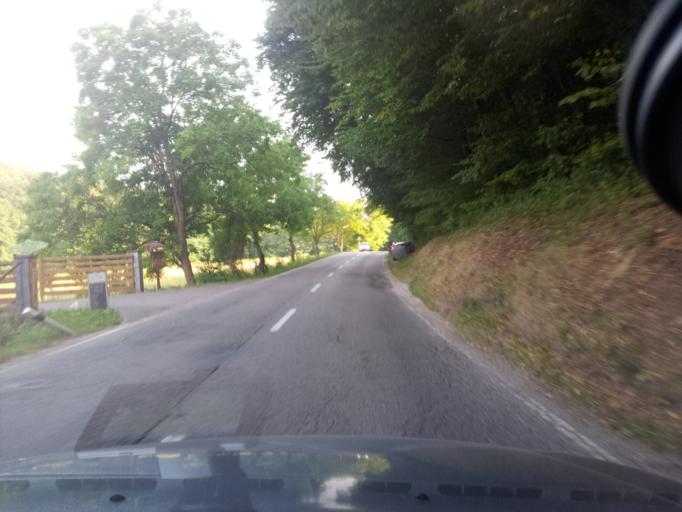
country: SK
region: Nitriansky
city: Trencianske Teplice
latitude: 48.8702
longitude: 18.1879
